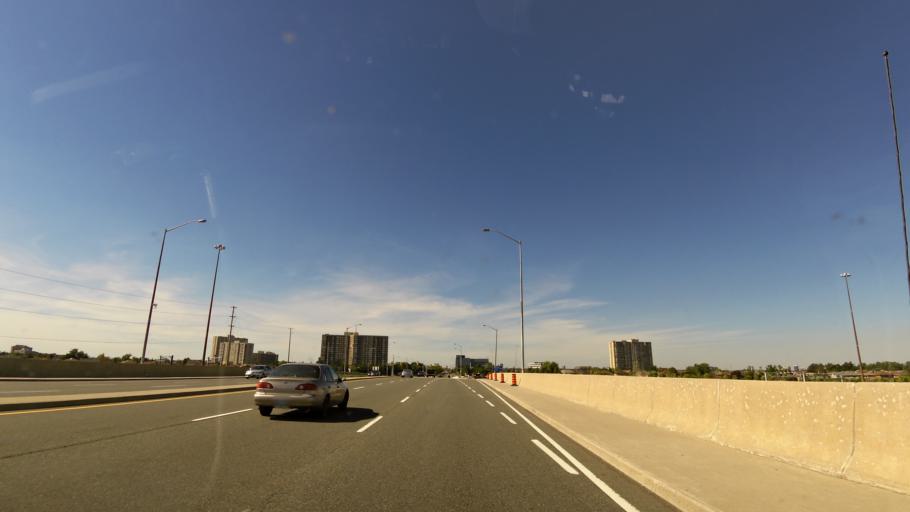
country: CA
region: Ontario
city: Brampton
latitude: 43.6534
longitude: -79.7160
